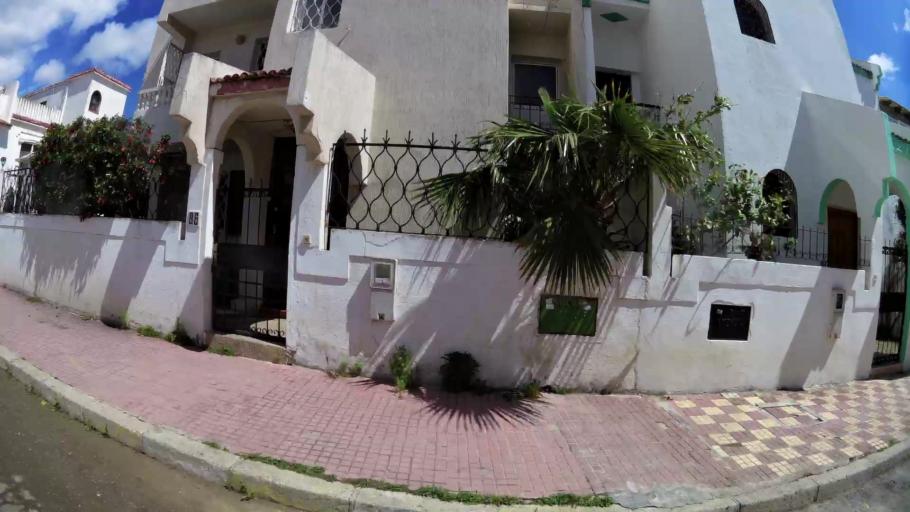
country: MA
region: Tanger-Tetouan
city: Tetouan
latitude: 35.5808
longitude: -5.3351
